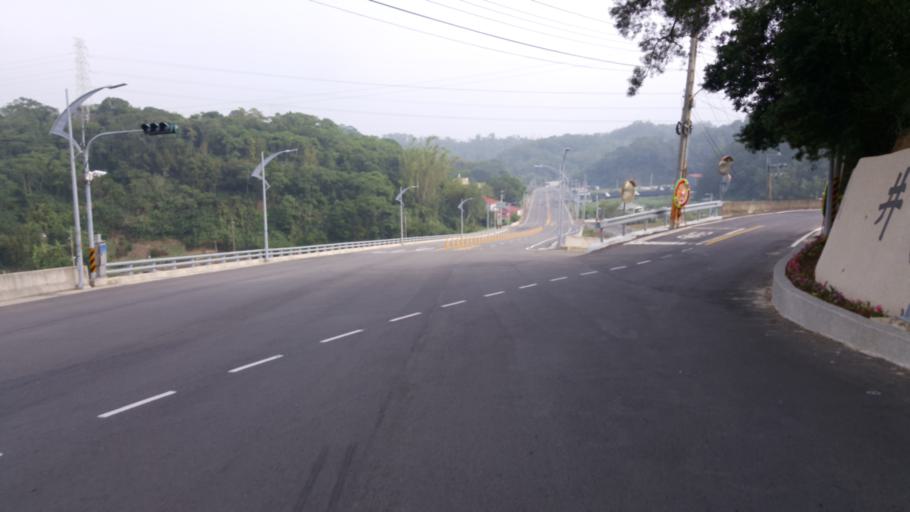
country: TW
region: Taiwan
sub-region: Hsinchu
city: Hsinchu
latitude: 24.7429
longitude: 120.9600
